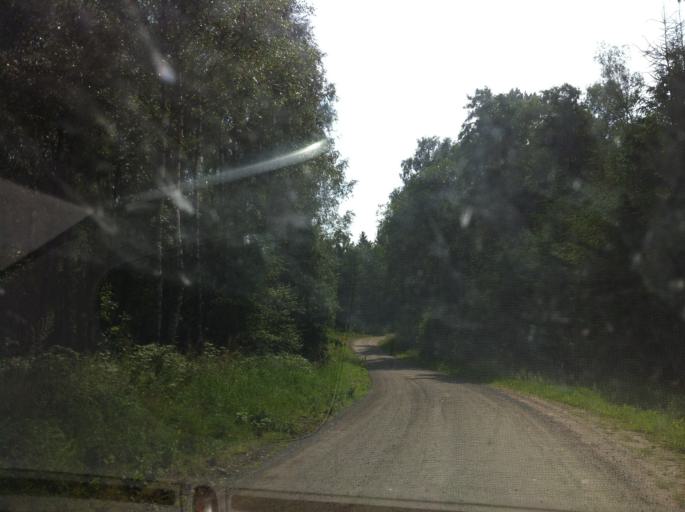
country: SE
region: Skane
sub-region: Eslovs Kommun
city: Stehag
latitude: 55.9773
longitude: 13.3899
